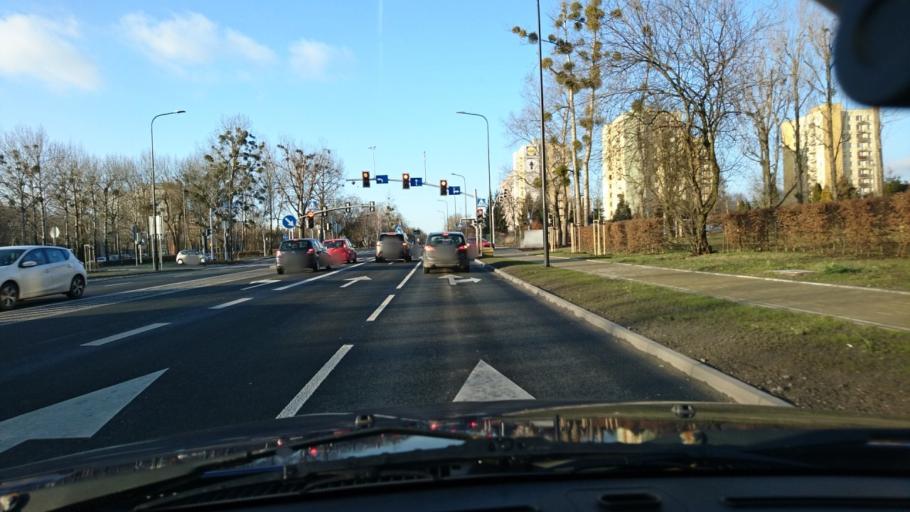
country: PL
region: Silesian Voivodeship
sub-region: Gliwice
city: Gliwice
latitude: 50.3163
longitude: 18.6664
